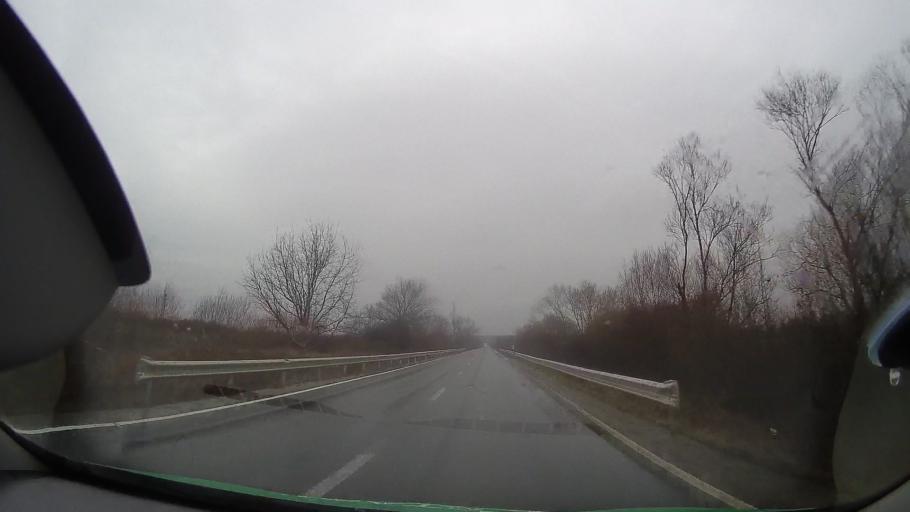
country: RO
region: Bihor
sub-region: Comuna Tinca
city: Tinca
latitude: 46.7574
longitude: 21.9357
